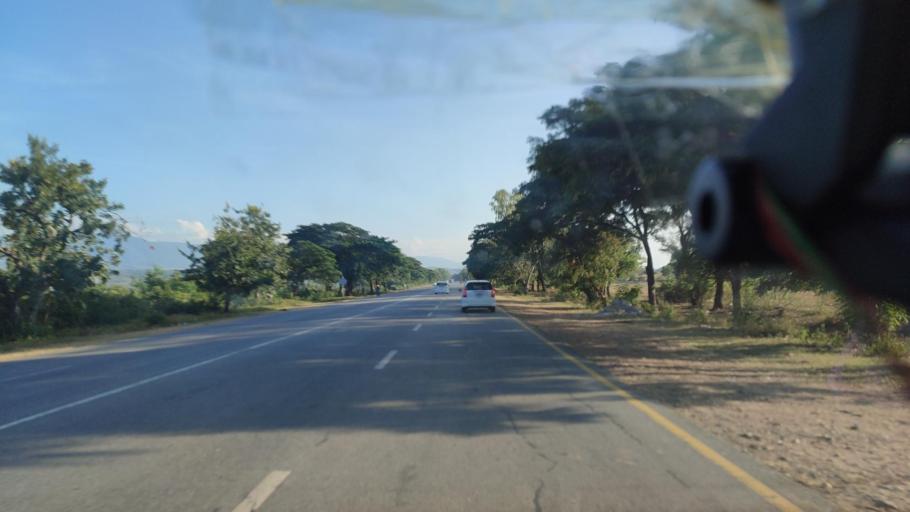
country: MM
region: Mandalay
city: Yamethin
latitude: 20.0982
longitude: 96.2442
